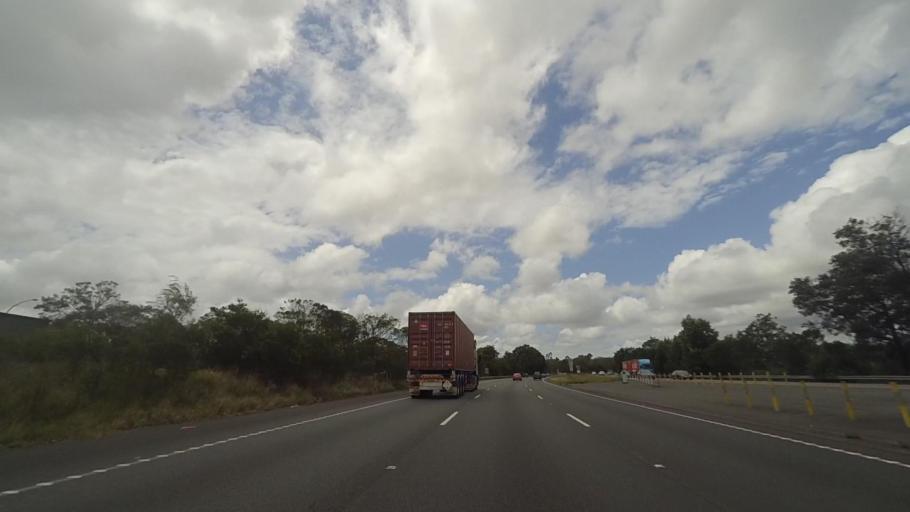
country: AU
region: New South Wales
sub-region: Gosford Shire
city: Point Clare
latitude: -33.4287
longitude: 151.2251
